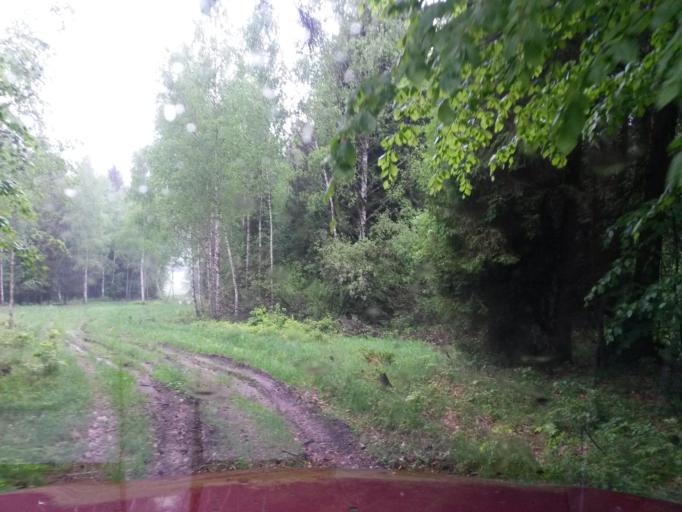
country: SK
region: Kosicky
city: Medzev
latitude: 48.7855
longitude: 20.7762
